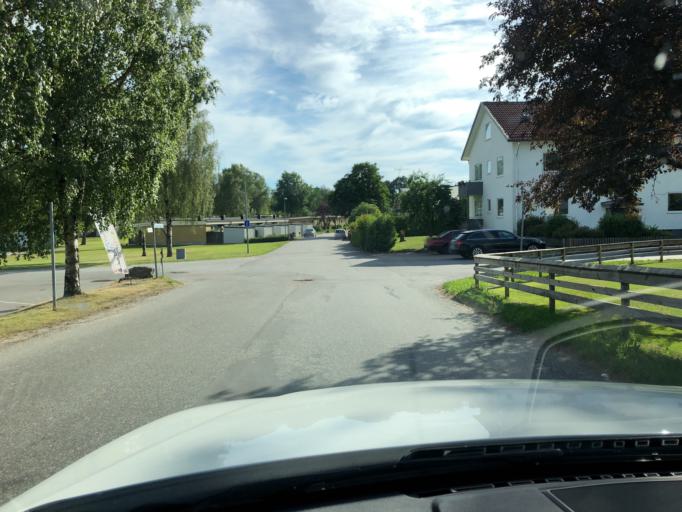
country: SE
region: Vaestra Goetaland
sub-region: Marks Kommun
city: Kinna
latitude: 57.4884
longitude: 12.6965
